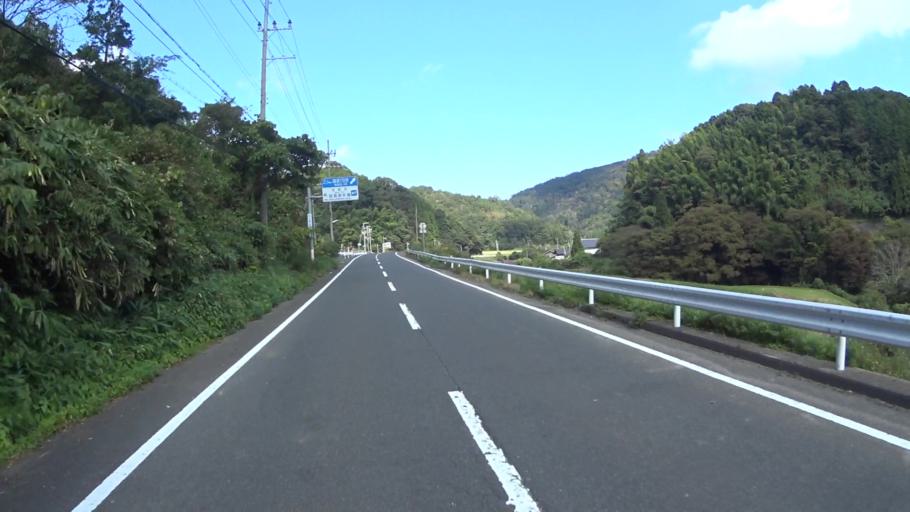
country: JP
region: Kyoto
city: Miyazu
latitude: 35.7022
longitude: 135.2500
